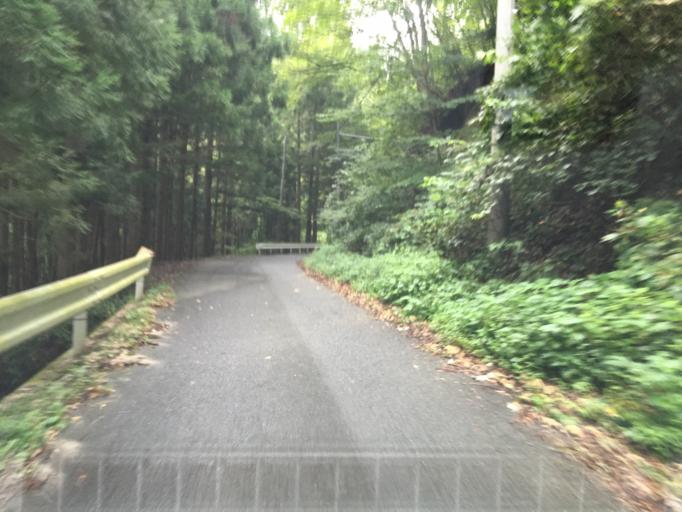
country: JP
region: Fukushima
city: Fukushima-shi
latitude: 37.7973
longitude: 140.3793
